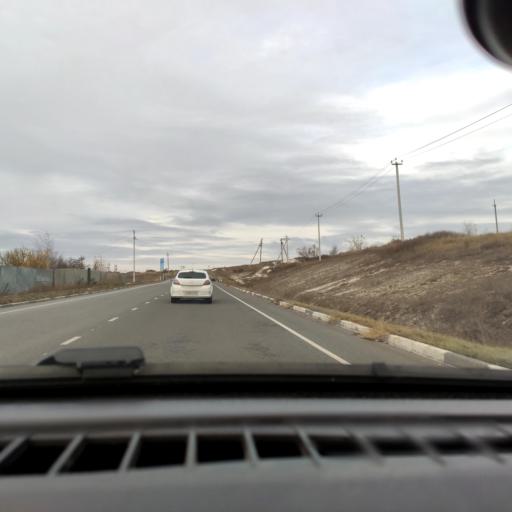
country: RU
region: Belgorod
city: Alekseyevka
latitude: 50.6443
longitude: 38.6439
